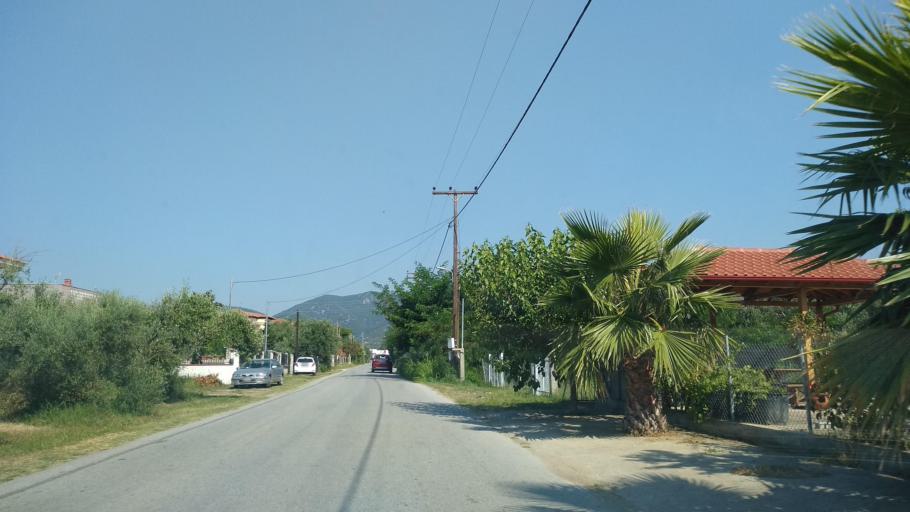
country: GR
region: Central Macedonia
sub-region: Nomos Thessalonikis
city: Nea Vrasna
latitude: 40.6906
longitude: 23.6862
